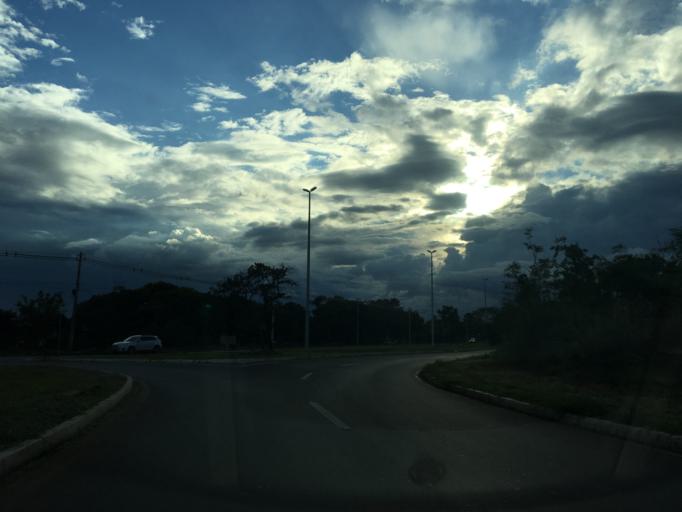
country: BR
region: Federal District
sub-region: Brasilia
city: Brasilia
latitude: -15.8138
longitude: -47.8491
